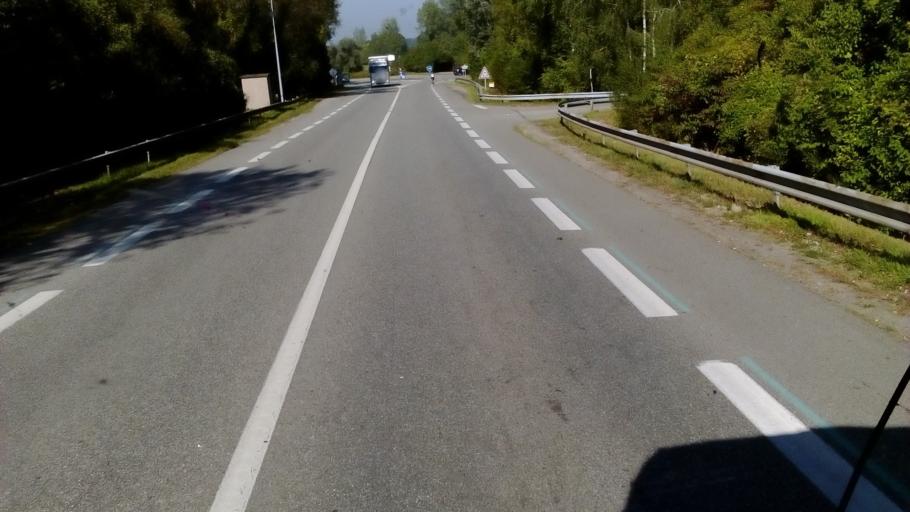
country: FR
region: Alsace
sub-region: Departement du Bas-Rhin
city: Gambsheim
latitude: 48.6885
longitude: 7.9080
